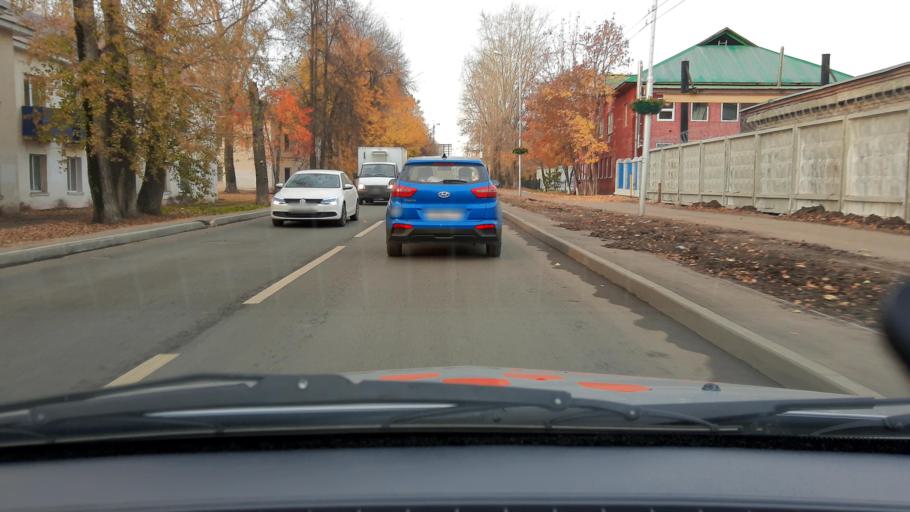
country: RU
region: Bashkortostan
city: Mikhaylovka
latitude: 54.7021
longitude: 55.8363
